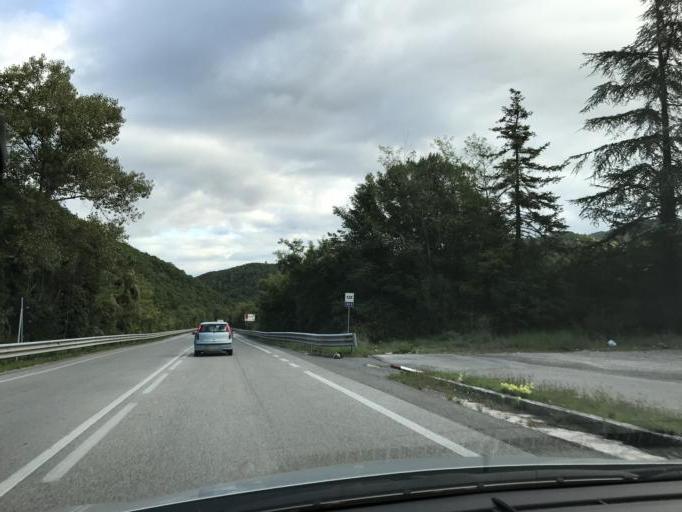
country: IT
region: Umbria
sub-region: Provincia di Perugia
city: Spoleto
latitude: 42.6935
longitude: 12.7215
